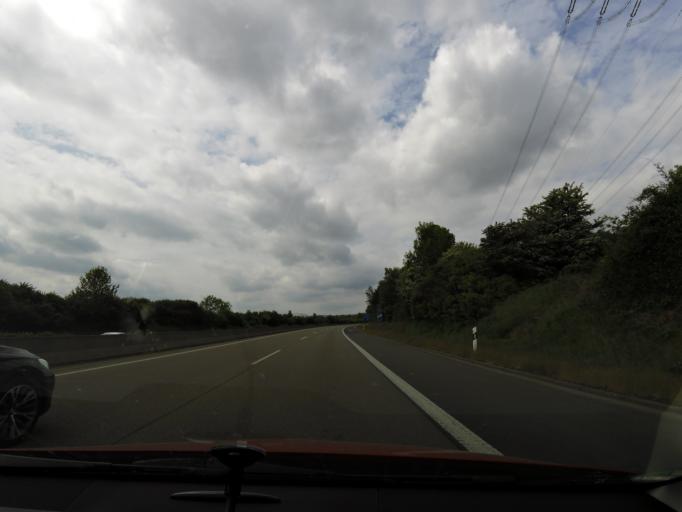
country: DE
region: Thuringia
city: Gerstungen
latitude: 50.9649
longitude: 10.0578
